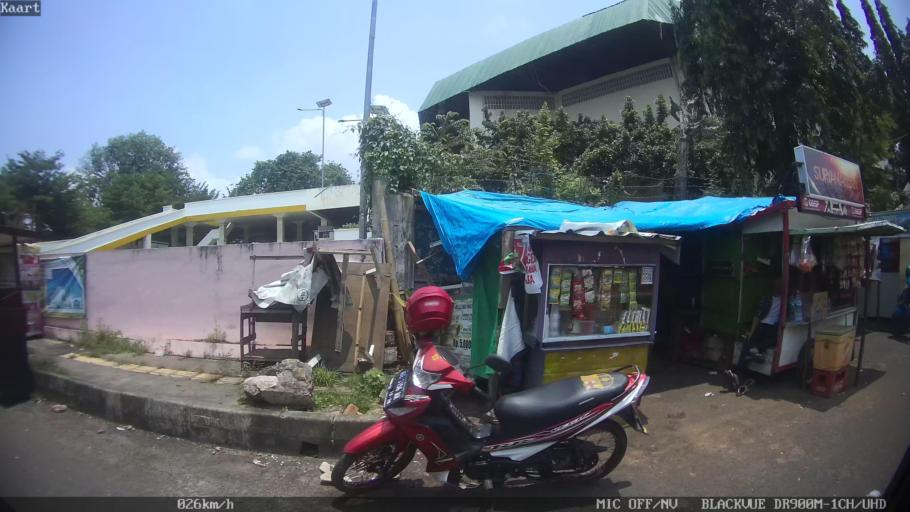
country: ID
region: Lampung
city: Bandarlampung
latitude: -5.4211
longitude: 105.2603
